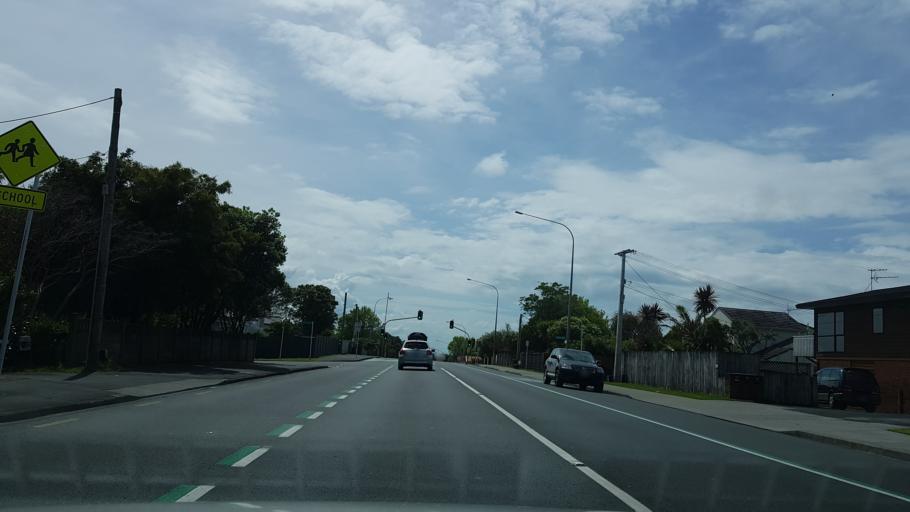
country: NZ
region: Auckland
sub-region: Auckland
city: North Shore
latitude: -36.8101
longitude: 174.7315
